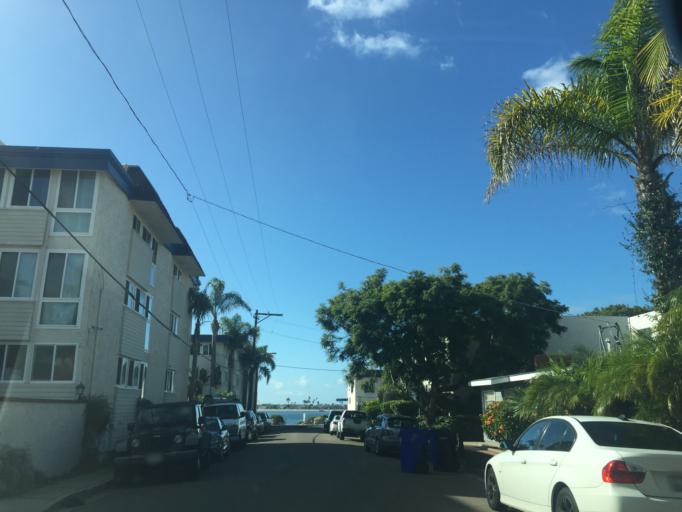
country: US
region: California
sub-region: San Diego County
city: La Jolla
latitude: 32.7906
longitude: -117.2411
